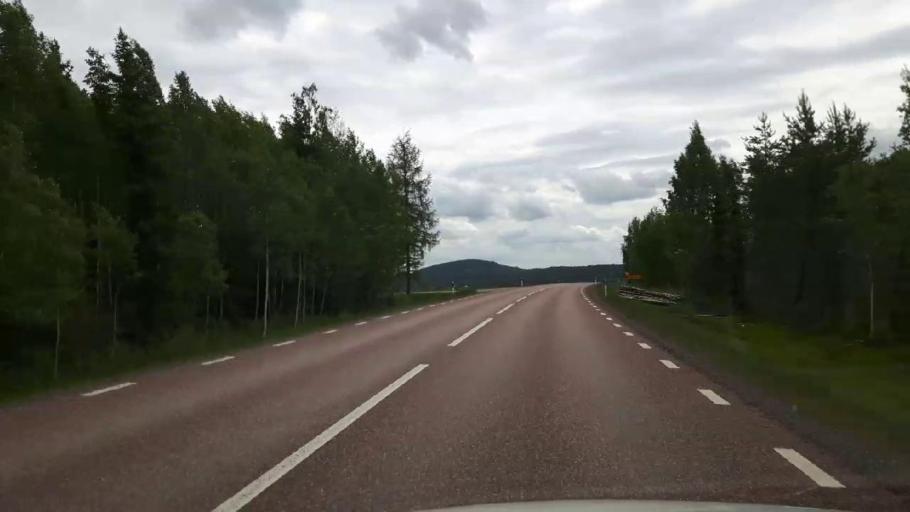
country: SE
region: Dalarna
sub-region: Hedemora Kommun
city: Brunna
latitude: 60.2479
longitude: 16.0105
